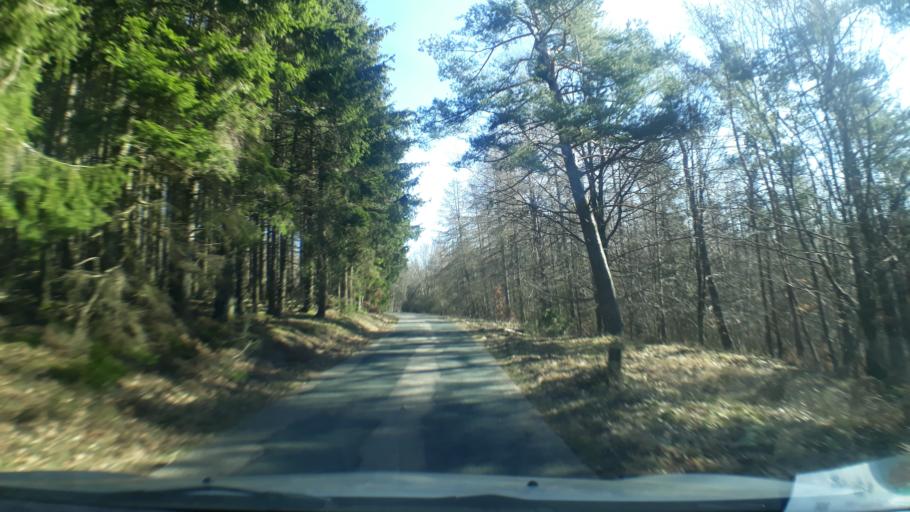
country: DE
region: North Rhine-Westphalia
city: Heimbach
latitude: 50.6120
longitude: 6.4354
